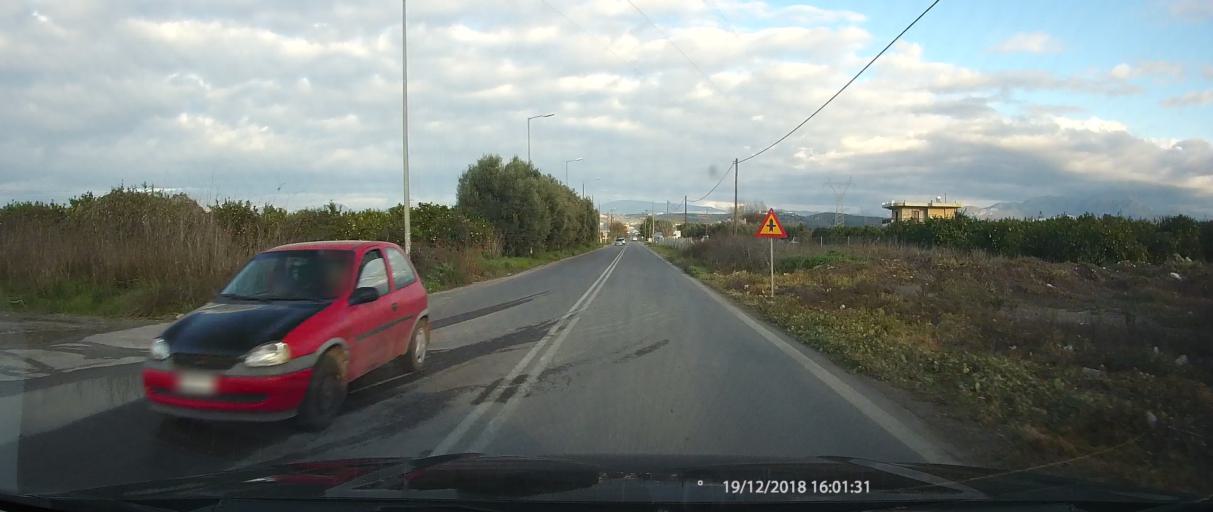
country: GR
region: Peloponnese
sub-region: Nomos Lakonias
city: Vlakhiotis
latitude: 36.8570
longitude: 22.6892
